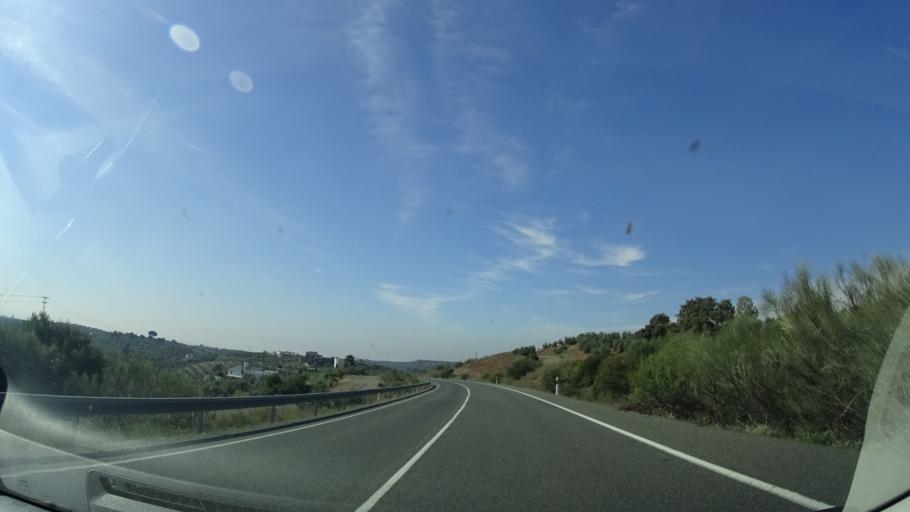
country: ES
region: Andalusia
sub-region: Province of Cordoba
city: Montoro
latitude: 38.0764
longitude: -4.3741
